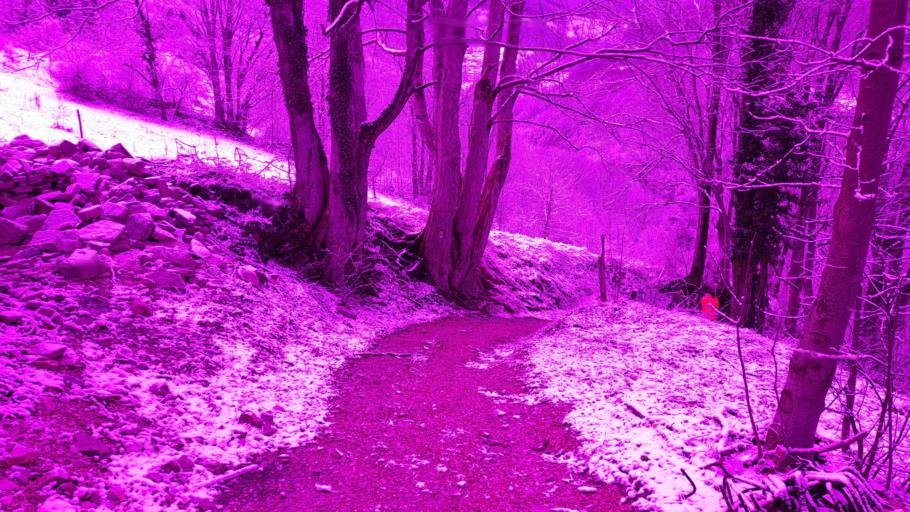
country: IT
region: The Marches
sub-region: Provincia di Macerata
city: Bolognola
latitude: 42.9879
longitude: 13.2309
